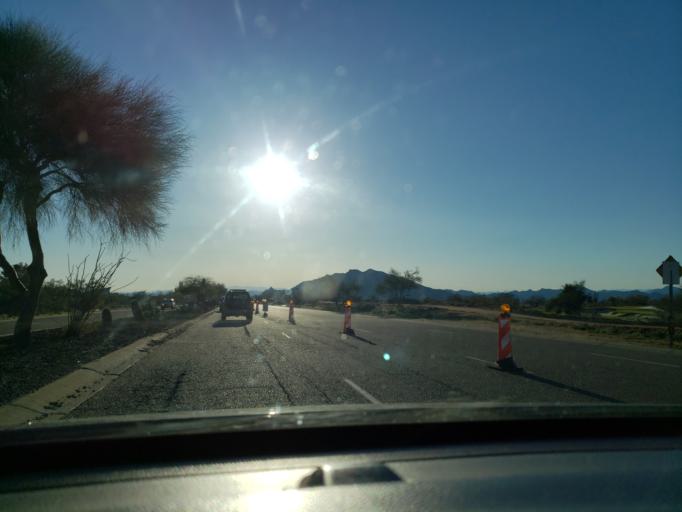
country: US
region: Arizona
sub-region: Maricopa County
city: Carefree
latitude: 33.8241
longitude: -111.8788
